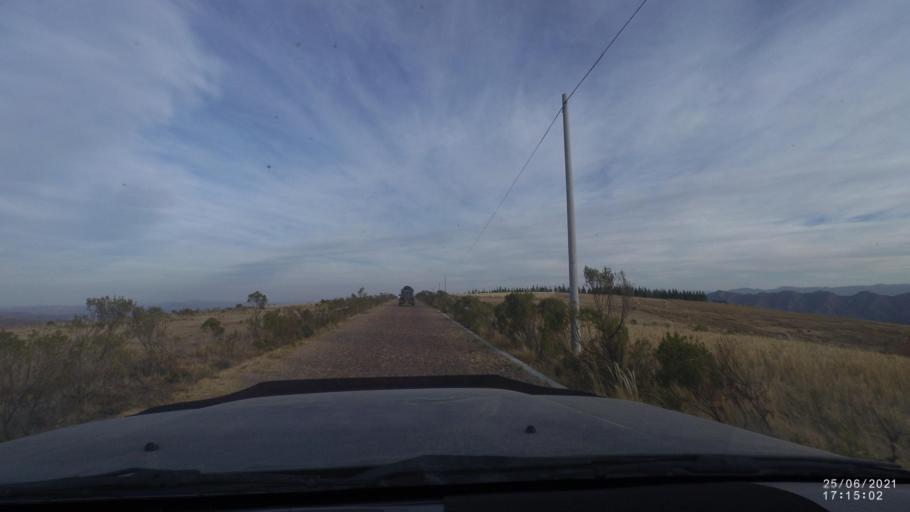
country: BO
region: Cochabamba
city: Arani
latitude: -17.8707
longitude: -65.6989
